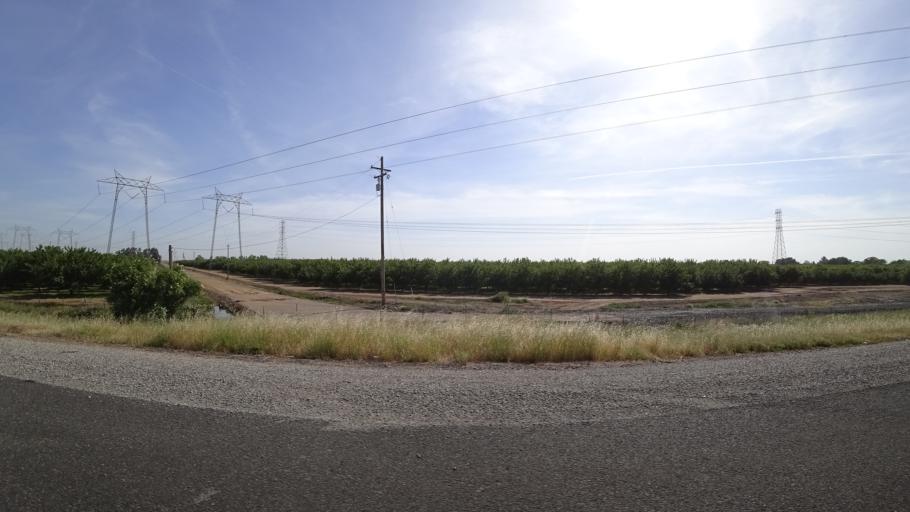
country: US
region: California
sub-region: Butte County
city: Thermalito
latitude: 39.6059
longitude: -121.6703
